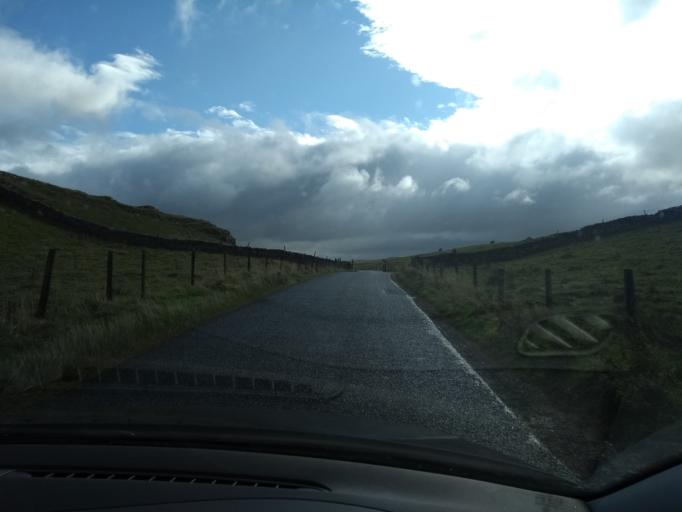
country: GB
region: England
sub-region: North Yorkshire
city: Settle
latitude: 54.0845
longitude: -2.1792
